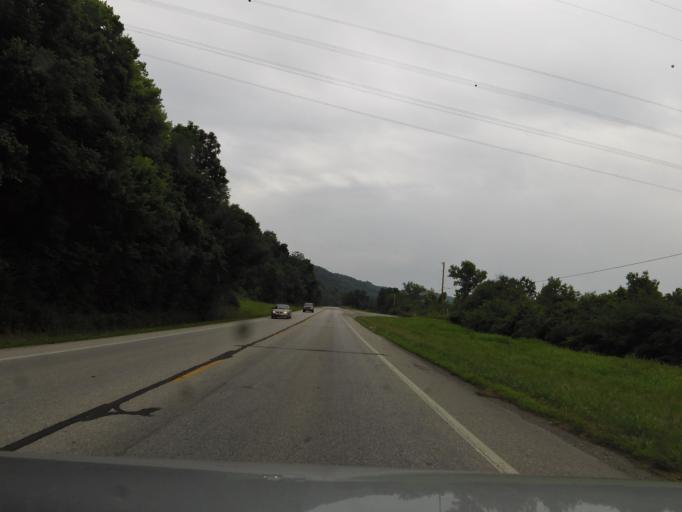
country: US
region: Ohio
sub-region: Brown County
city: Aberdeen
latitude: 38.7034
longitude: -83.7920
